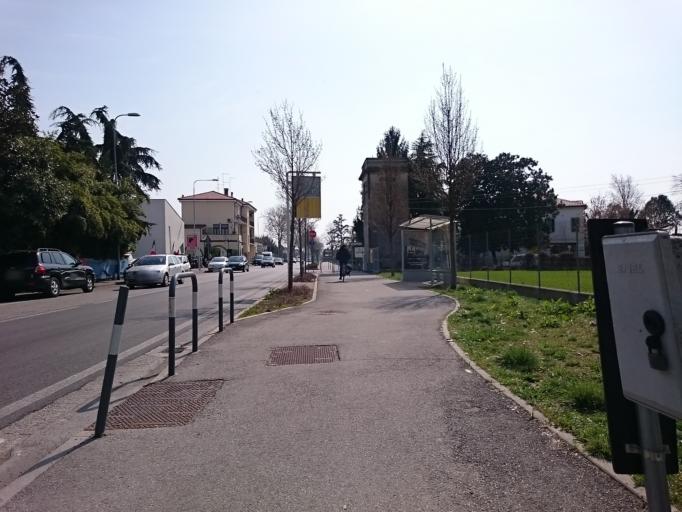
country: IT
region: Veneto
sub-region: Provincia di Padova
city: Albignasego
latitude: 45.3758
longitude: 11.8863
